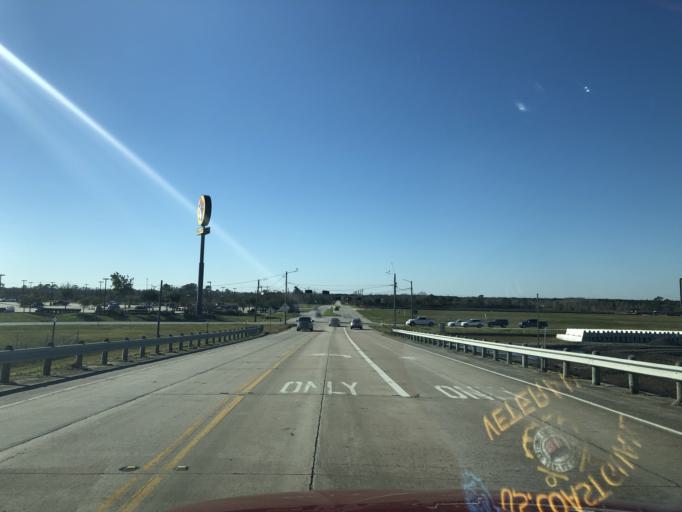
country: US
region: Texas
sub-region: Galveston County
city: Dickinson
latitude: 29.4304
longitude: -95.0616
